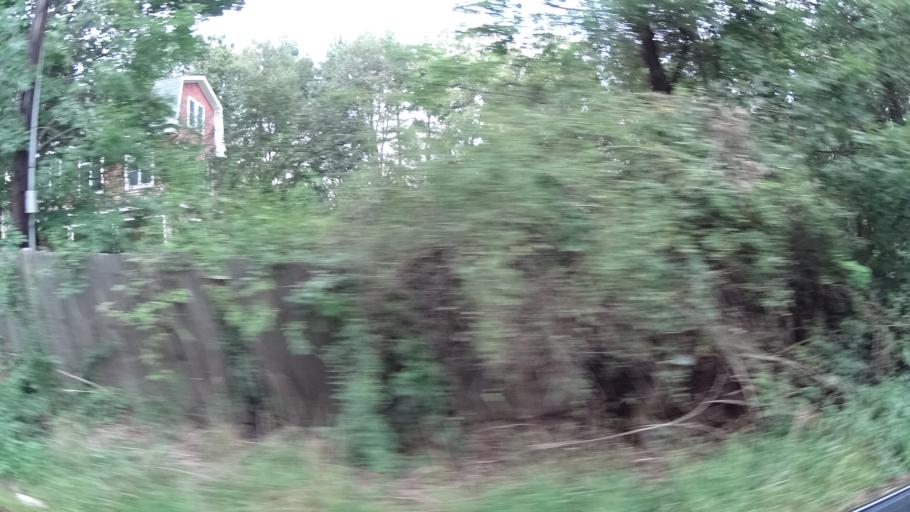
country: US
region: New Jersey
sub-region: Morris County
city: Madison
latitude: 40.7400
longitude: -74.4604
